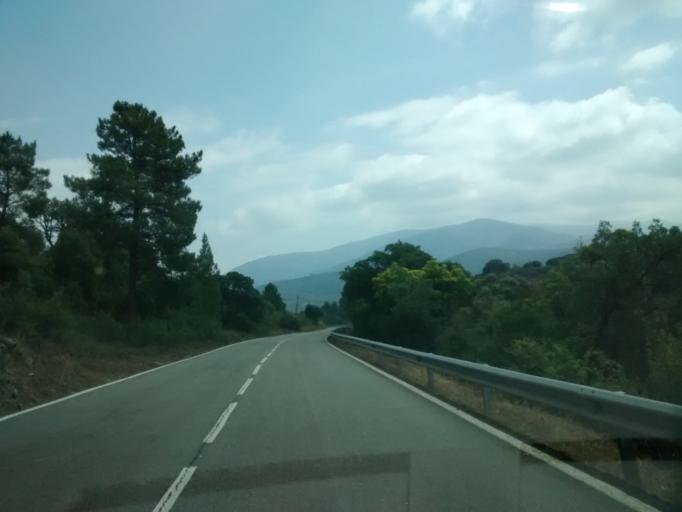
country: ES
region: Galicia
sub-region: Provincia de Ourense
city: Petin
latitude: 42.3507
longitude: -7.1533
